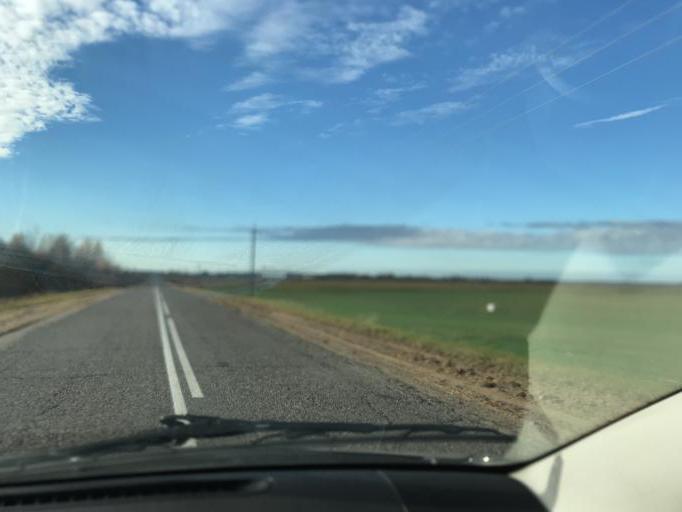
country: BY
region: Vitebsk
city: Haradok
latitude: 55.3828
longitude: 29.6513
